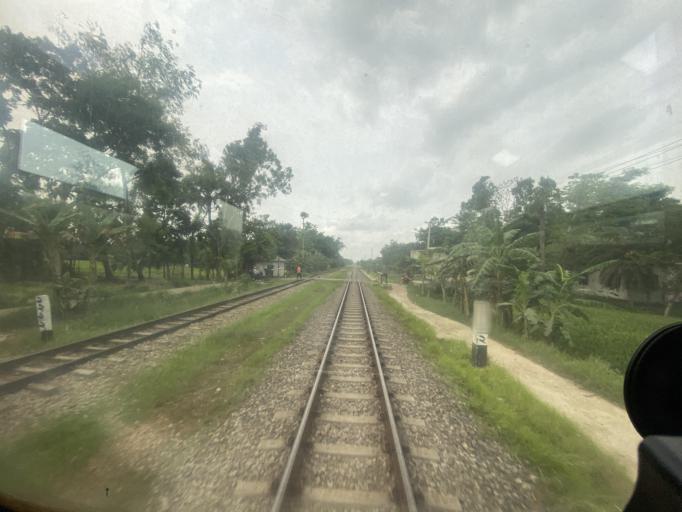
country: BD
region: Chittagong
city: Laksham
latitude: 23.1953
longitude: 91.1659
